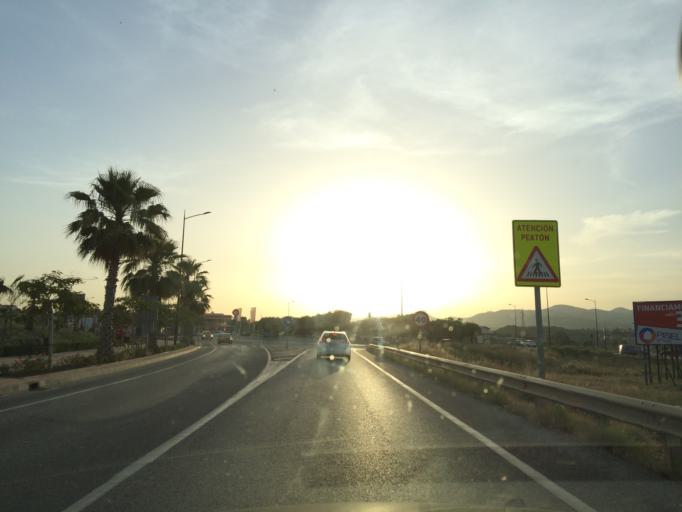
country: ES
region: Andalusia
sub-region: Provincia de Malaga
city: Alhaurin de la Torre
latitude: 36.6704
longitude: -4.5533
